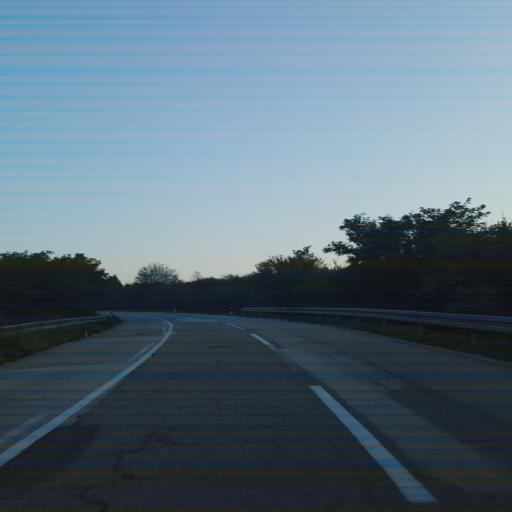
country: RS
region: Central Serbia
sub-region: Zajecarski Okrug
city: Zajecar
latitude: 43.9930
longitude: 22.3019
